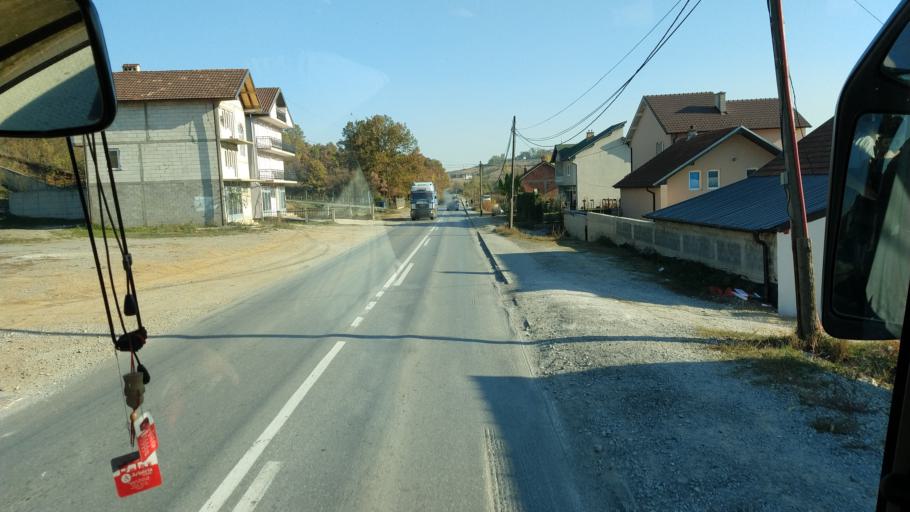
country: XK
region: Ferizaj
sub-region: Komuna e Shtimes
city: Shtime
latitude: 42.4416
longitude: 21.0148
